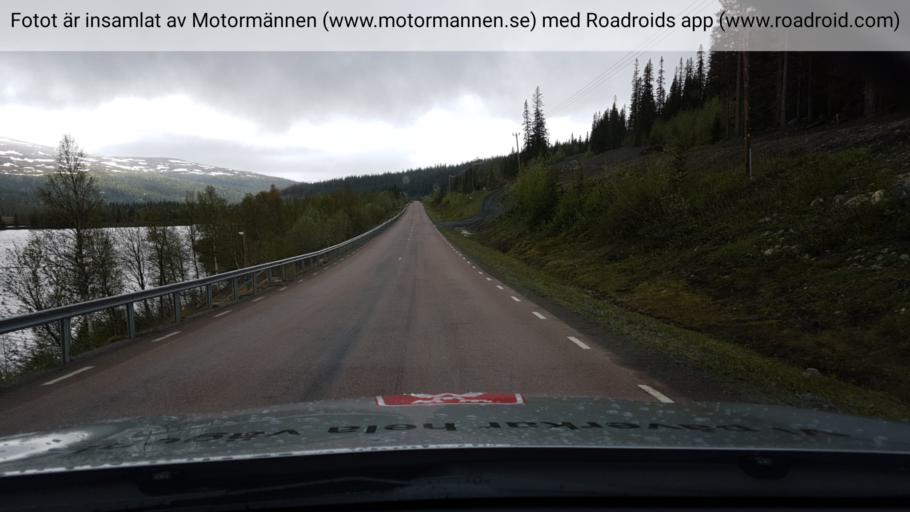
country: SE
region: Jaemtland
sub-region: Are Kommun
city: Jarpen
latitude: 63.0988
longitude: 13.7893
